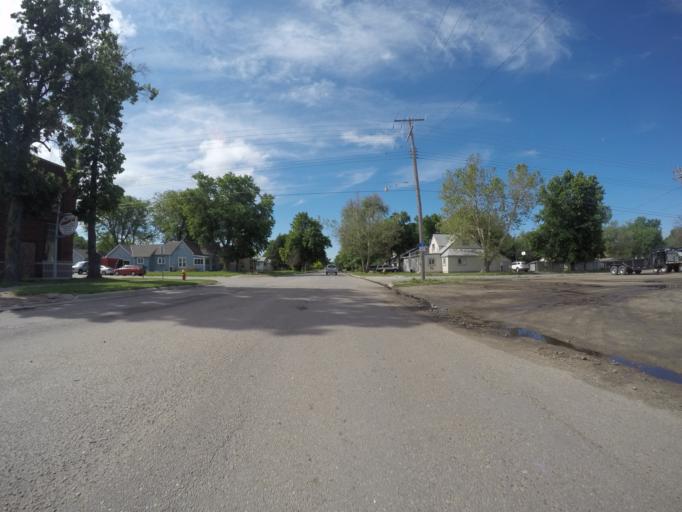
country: US
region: Nebraska
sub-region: Buffalo County
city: Kearney
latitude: 40.6938
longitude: -99.0887
